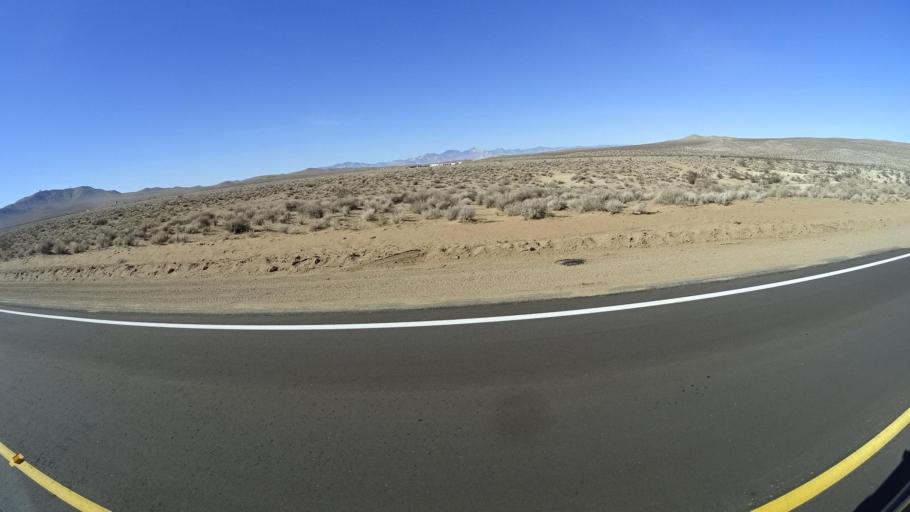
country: US
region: California
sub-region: Kern County
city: Ridgecrest
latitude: 35.4965
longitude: -117.6259
